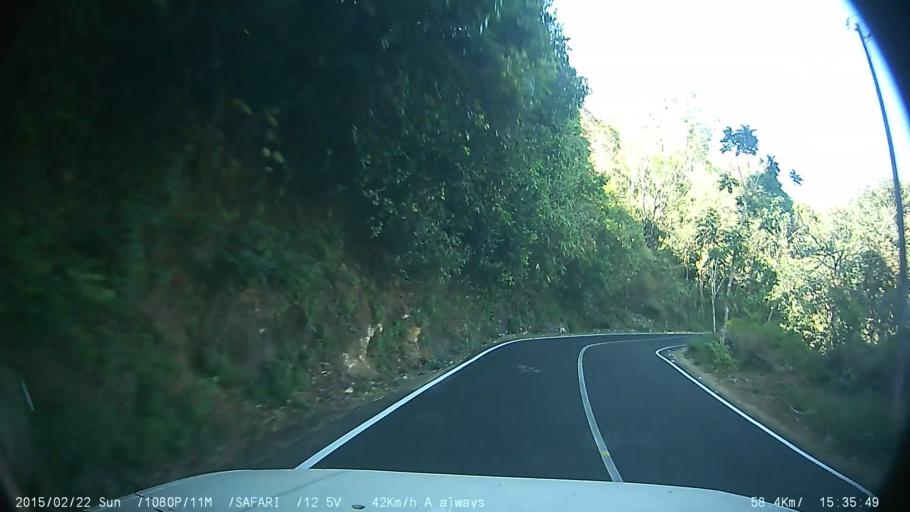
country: IN
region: Kerala
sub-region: Kottayam
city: Erattupetta
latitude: 9.5602
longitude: 76.9771
